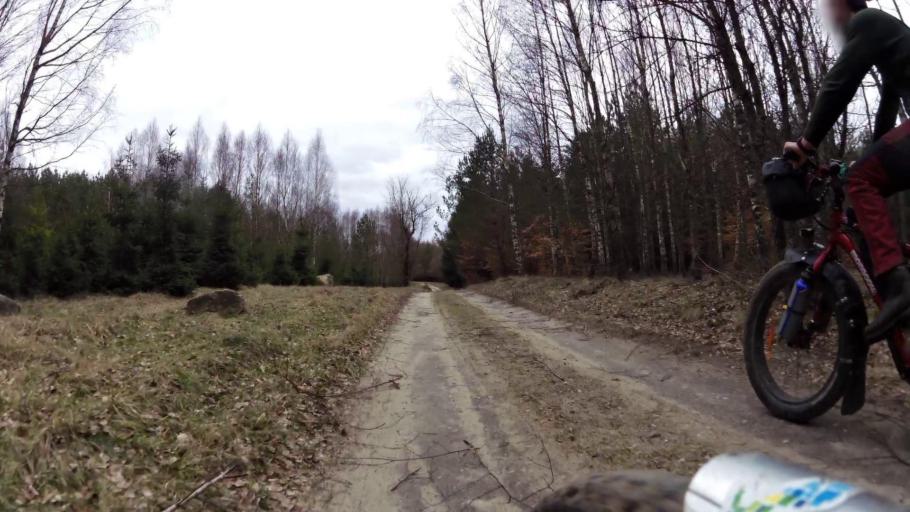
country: PL
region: Pomeranian Voivodeship
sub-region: Powiat bytowski
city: Trzebielino
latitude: 54.1161
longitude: 17.1280
